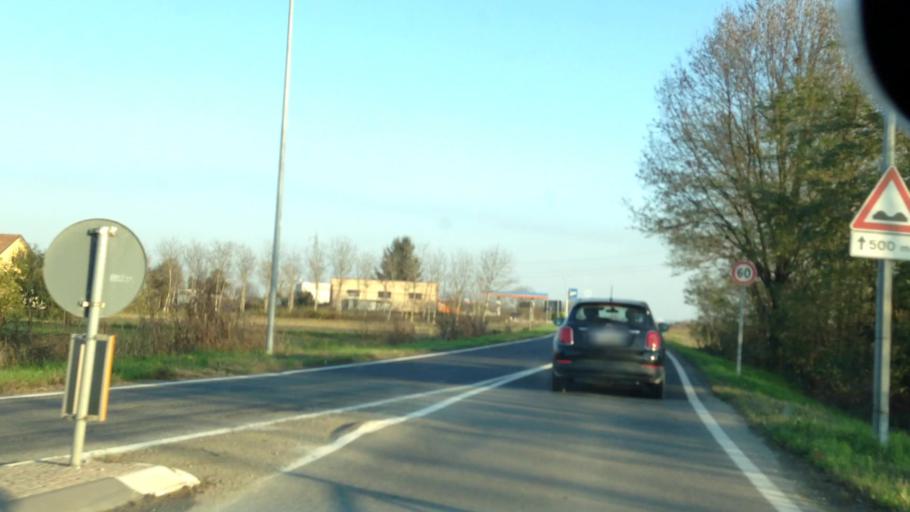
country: IT
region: Piedmont
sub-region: Provincia di Vercelli
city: Livorno Ferraris
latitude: 45.2736
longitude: 8.0766
